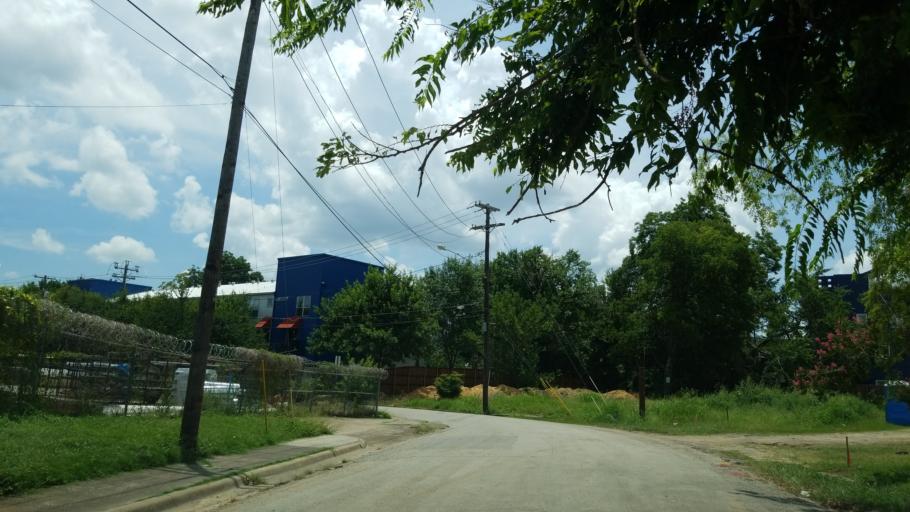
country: US
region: Texas
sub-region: Dallas County
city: Dallas
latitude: 32.7976
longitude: -96.7836
